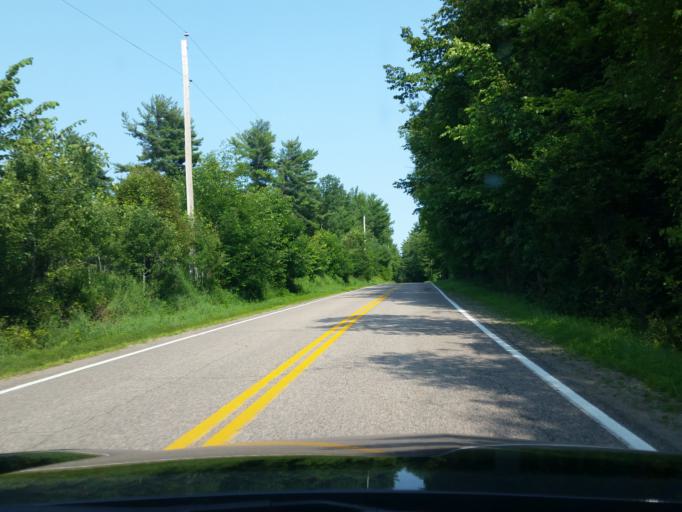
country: CA
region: Quebec
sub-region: Outaouais
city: Shawville
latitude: 45.5232
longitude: -76.4435
